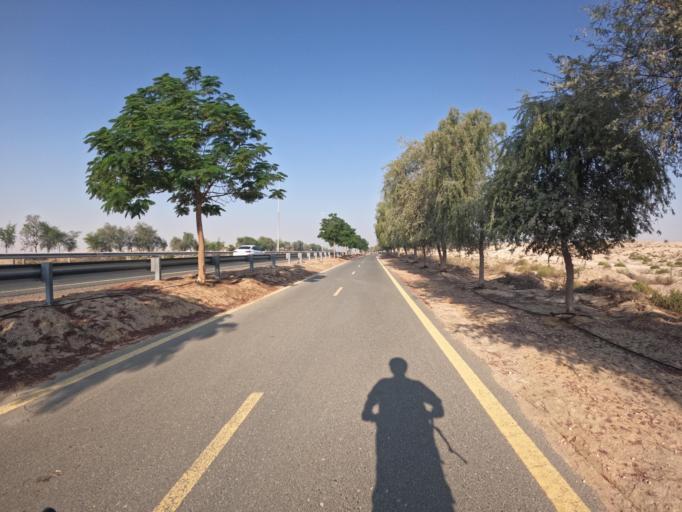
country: AE
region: Dubai
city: Dubai
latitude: 24.9858
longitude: 55.3257
